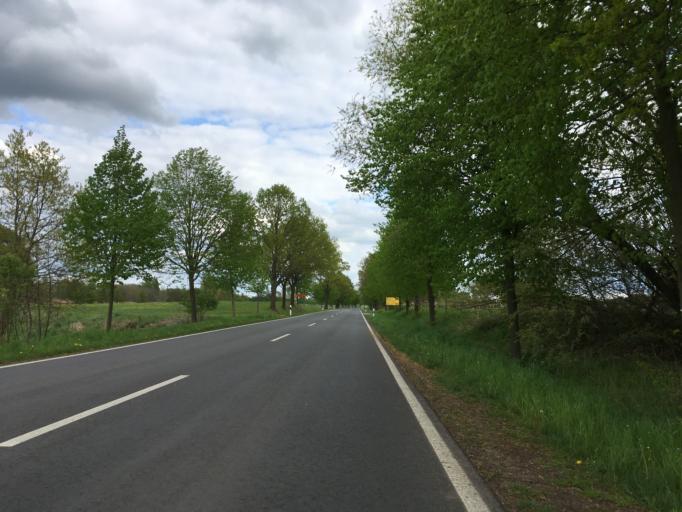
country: DE
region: Brandenburg
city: Bernau bei Berlin
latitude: 52.6652
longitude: 13.5866
